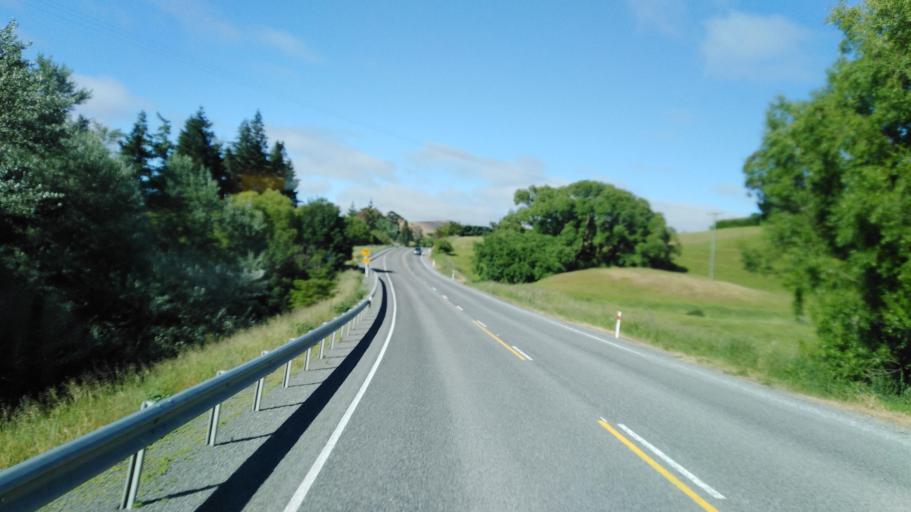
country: NZ
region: Canterbury
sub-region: Hurunui District
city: Amberley
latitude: -43.0060
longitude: 172.7048
